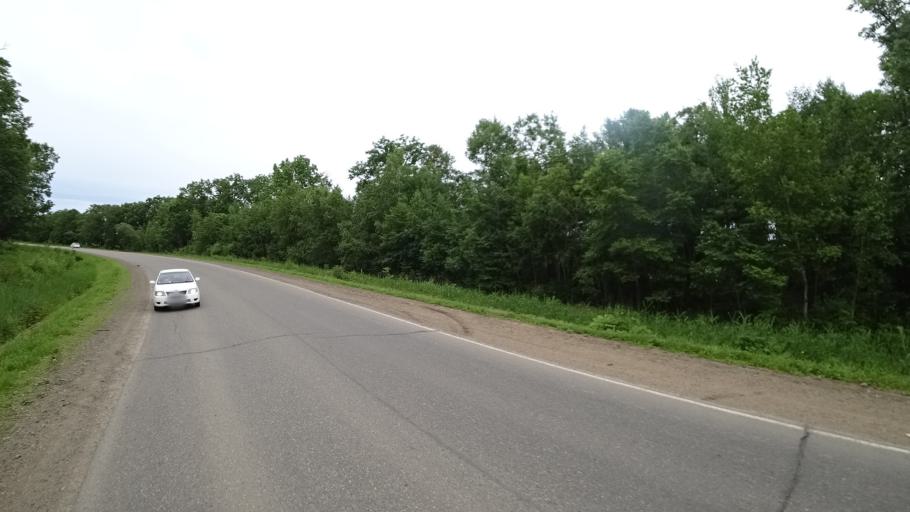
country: RU
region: Primorskiy
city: Novosysoyevka
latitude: 44.1883
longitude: 133.3546
